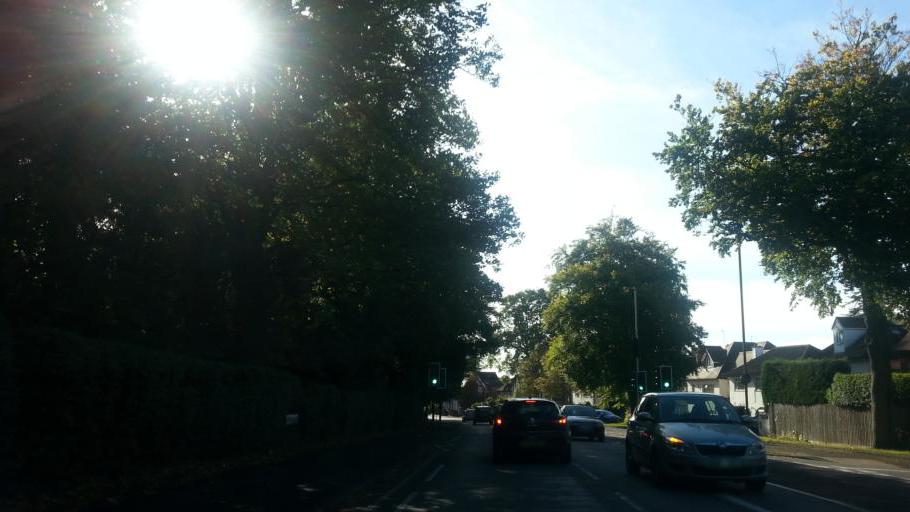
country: GB
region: England
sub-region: Leicestershire
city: Oadby
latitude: 52.6107
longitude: -1.1006
